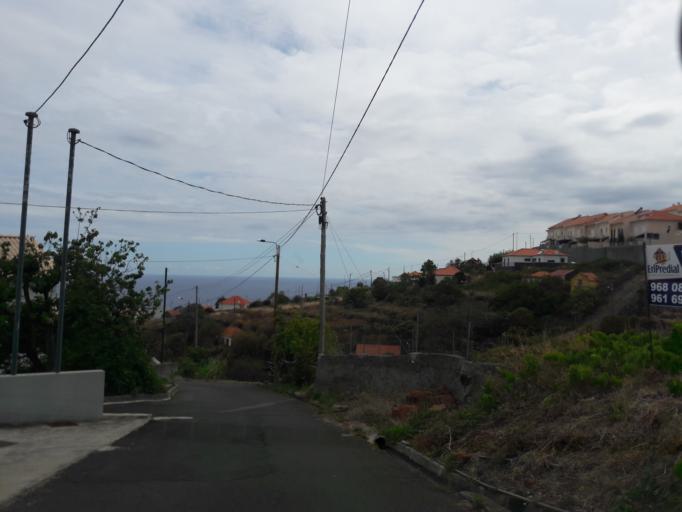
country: PT
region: Madeira
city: Canico
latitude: 32.6446
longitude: -16.8415
